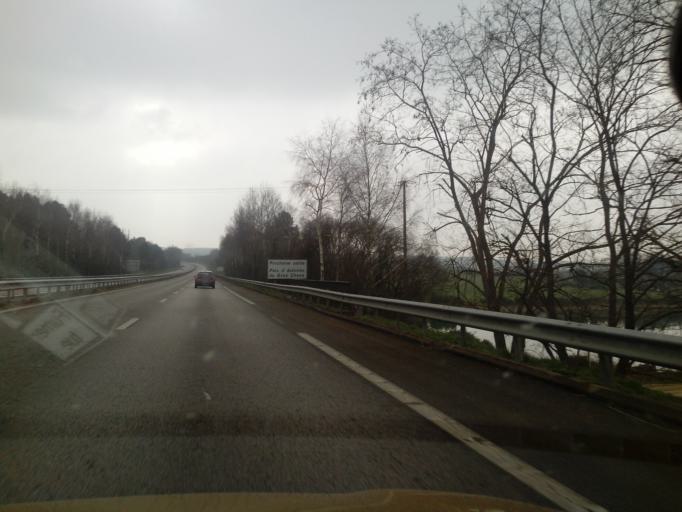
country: FR
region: Brittany
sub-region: Departement du Morbihan
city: Malestroit
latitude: 47.8331
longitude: -2.4301
